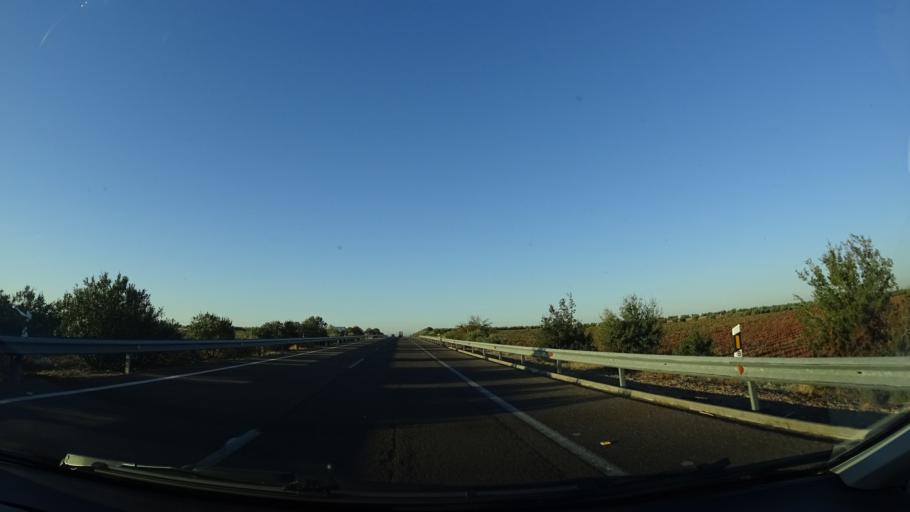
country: ES
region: Extremadura
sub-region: Provincia de Badajoz
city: Calamonte
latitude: 38.8070
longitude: -6.3803
